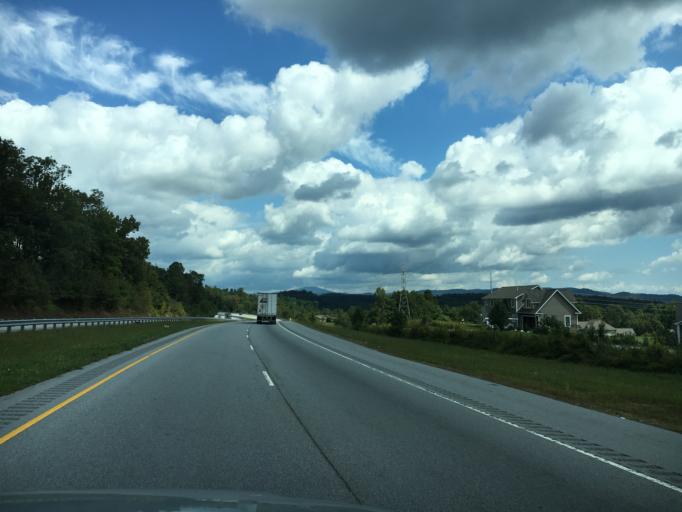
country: US
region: North Carolina
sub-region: Henderson County
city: East Flat Rock
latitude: 35.2665
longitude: -82.4046
